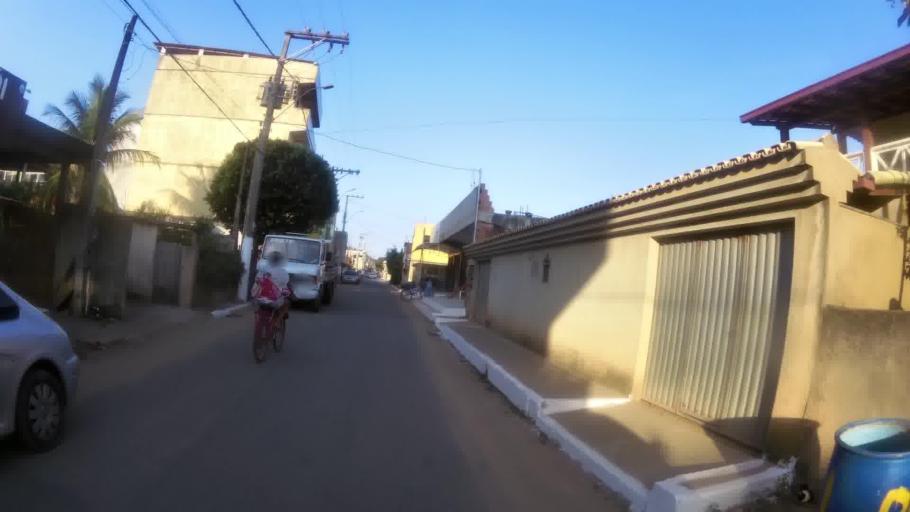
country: BR
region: Espirito Santo
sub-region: Piuma
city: Piuma
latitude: -20.8899
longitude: -40.7795
